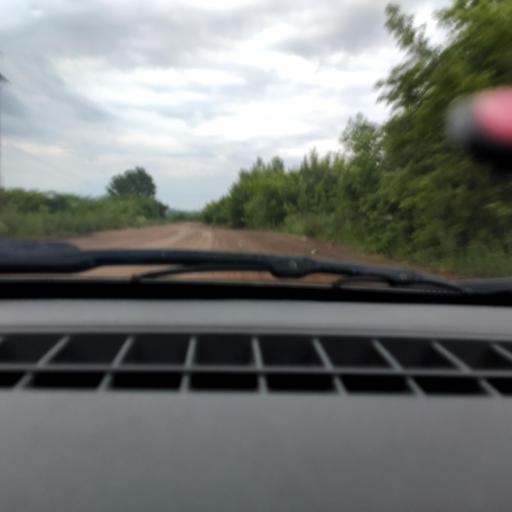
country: RU
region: Bashkortostan
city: Blagoveshchensk
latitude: 54.9180
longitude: 55.9810
